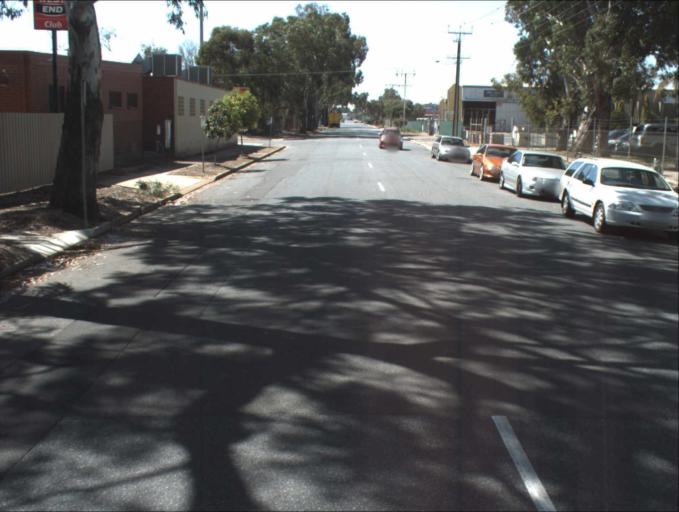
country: AU
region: South Australia
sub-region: Charles Sturt
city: Woodville North
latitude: -34.8484
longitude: 138.5599
